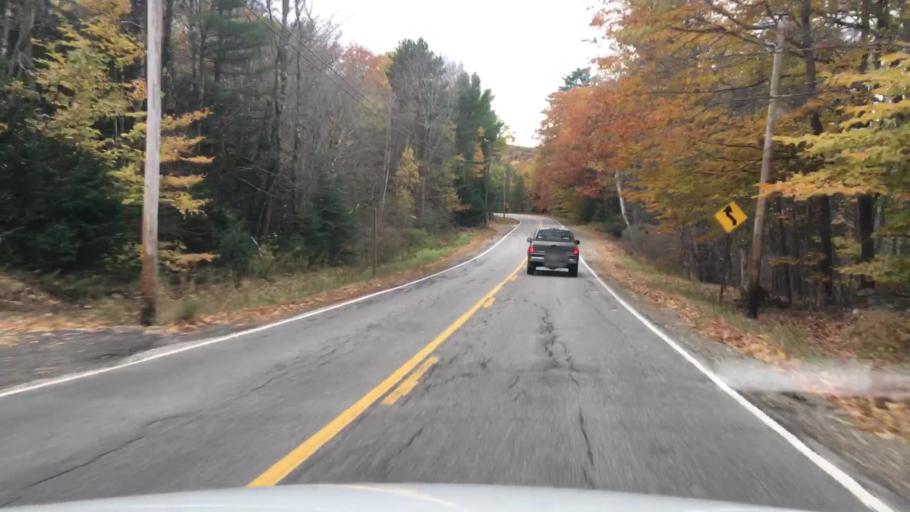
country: US
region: Maine
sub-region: Androscoggin County
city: Sabattus
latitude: 44.1356
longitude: -70.0020
